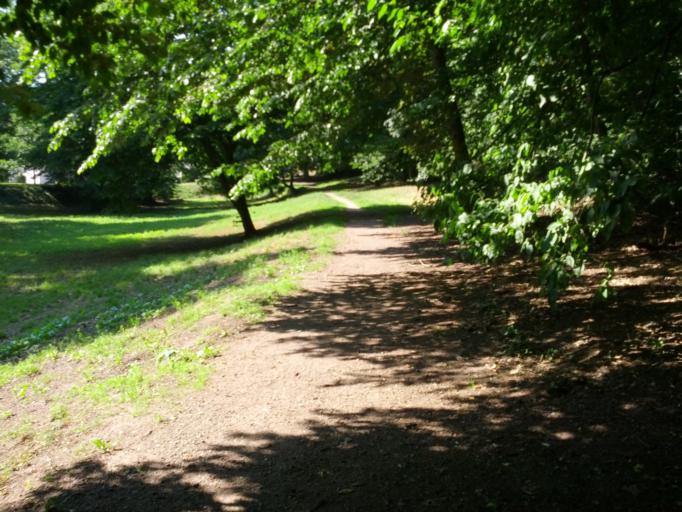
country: DE
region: Thuringia
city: Eisenach
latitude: 50.9650
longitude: 10.3243
